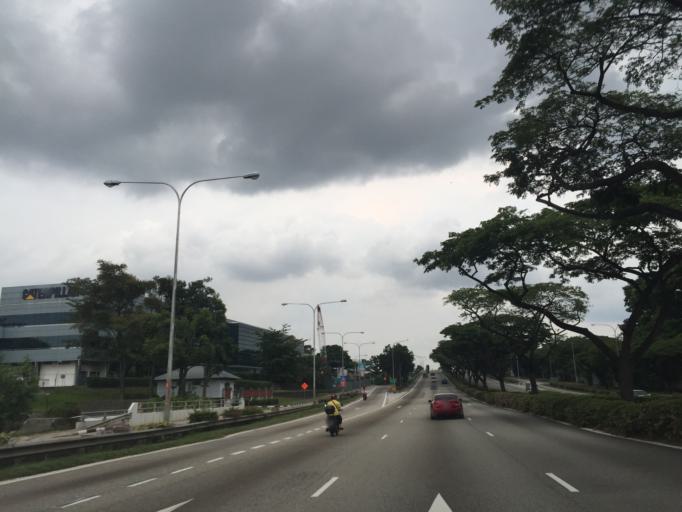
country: SG
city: Singapore
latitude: 1.3221
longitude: 103.7036
